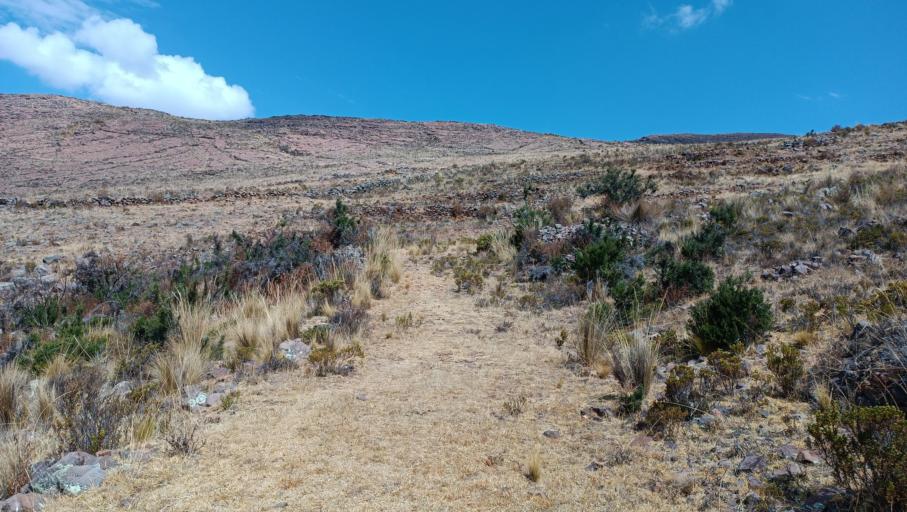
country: BO
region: La Paz
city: Batallas
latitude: -16.3498
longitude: -68.6500
